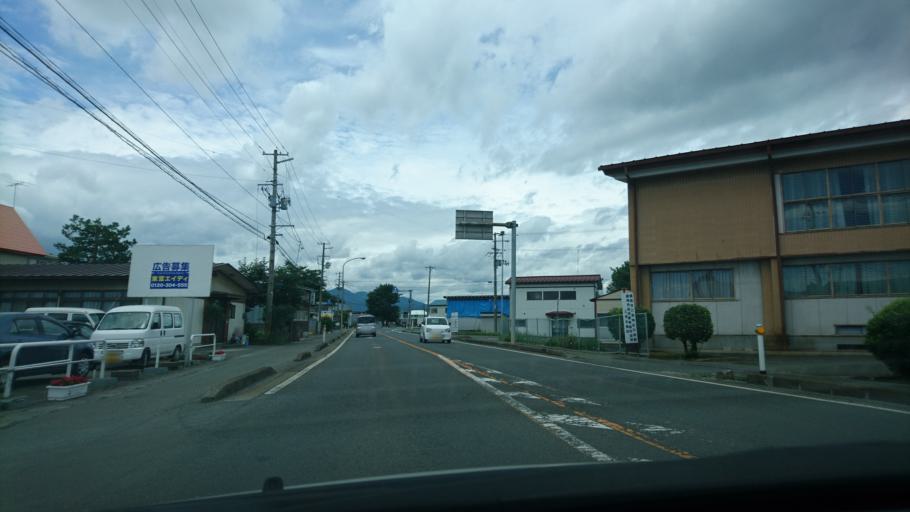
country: JP
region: Iwate
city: Morioka-shi
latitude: 39.6157
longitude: 141.1934
